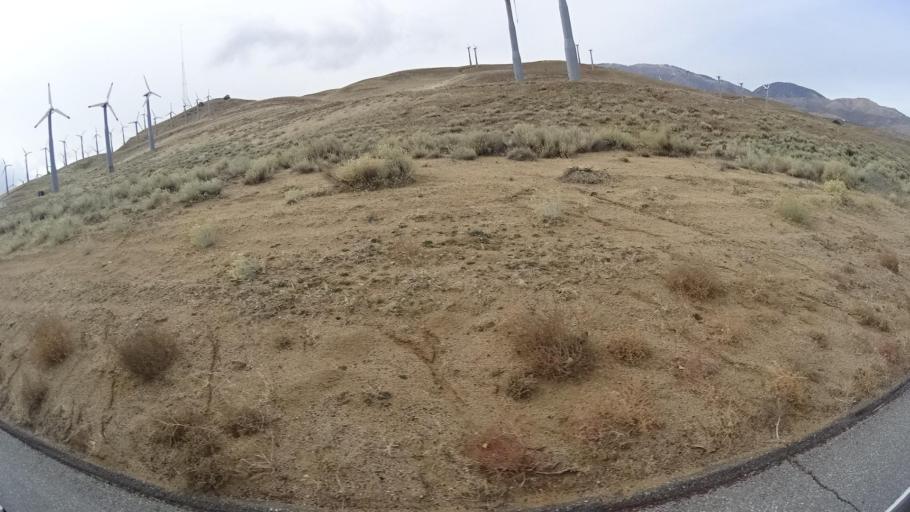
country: US
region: California
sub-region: Kern County
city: Tehachapi
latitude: 35.0627
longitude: -118.3906
